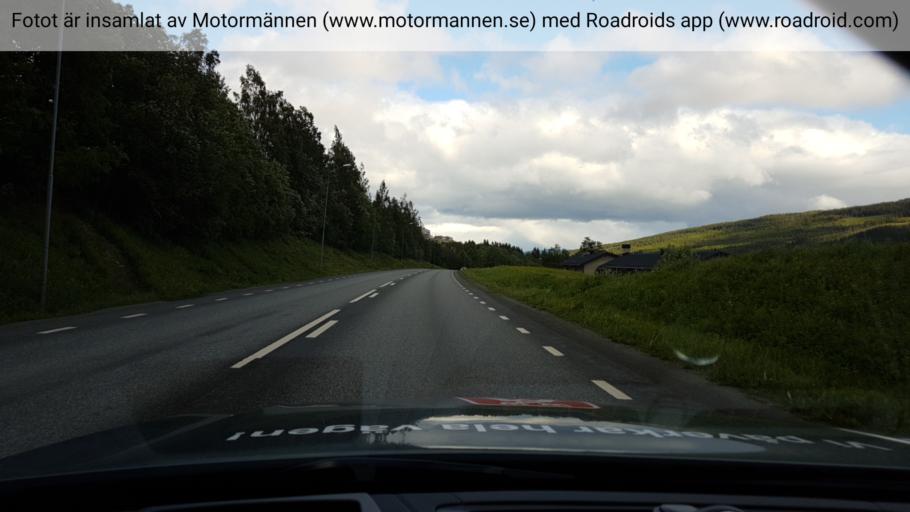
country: SE
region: Jaemtland
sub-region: Are Kommun
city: Are
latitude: 63.3989
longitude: 13.0850
